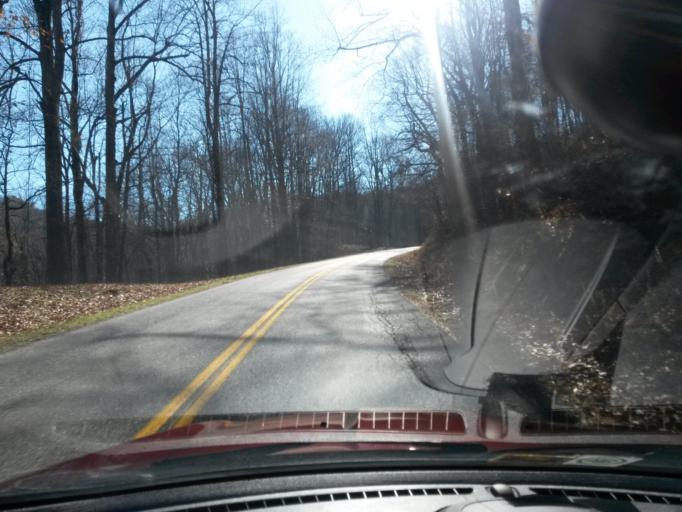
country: US
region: Virginia
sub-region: Botetourt County
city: Buchanan
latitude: 37.4591
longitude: -79.6299
